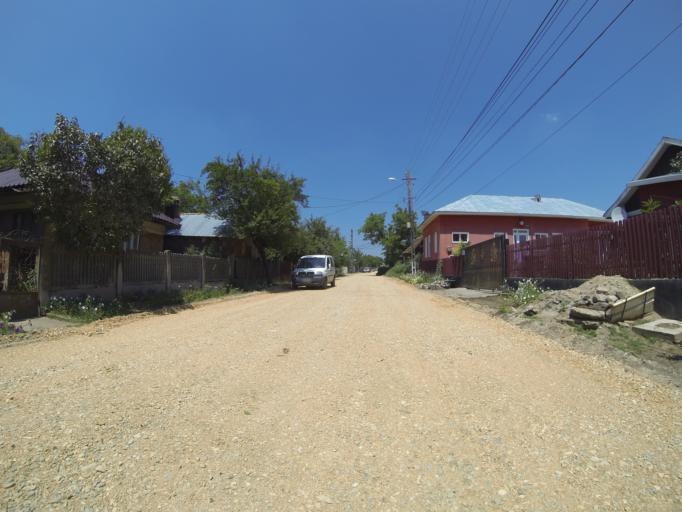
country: RO
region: Dolj
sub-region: Comuna Segarcea
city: Segarcea
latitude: 44.0905
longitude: 23.7489
